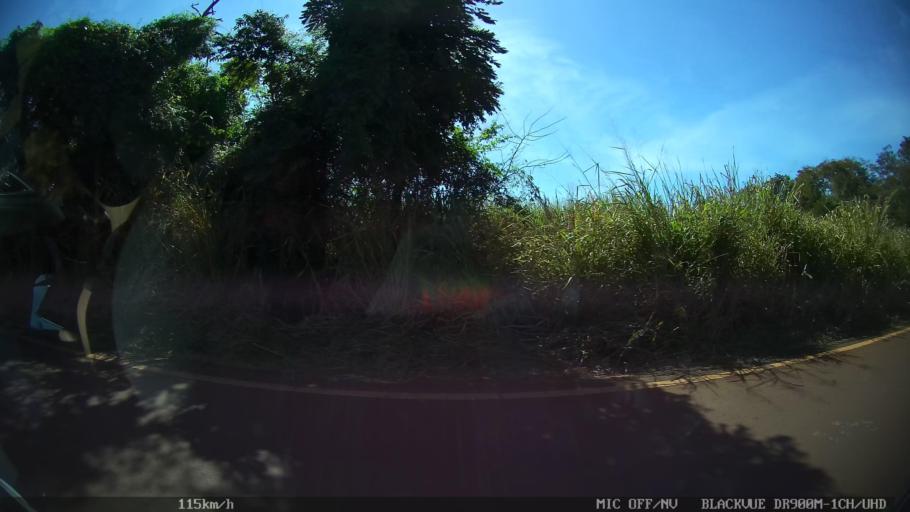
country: BR
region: Sao Paulo
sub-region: Guaira
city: Guaira
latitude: -20.4453
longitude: -48.2220
